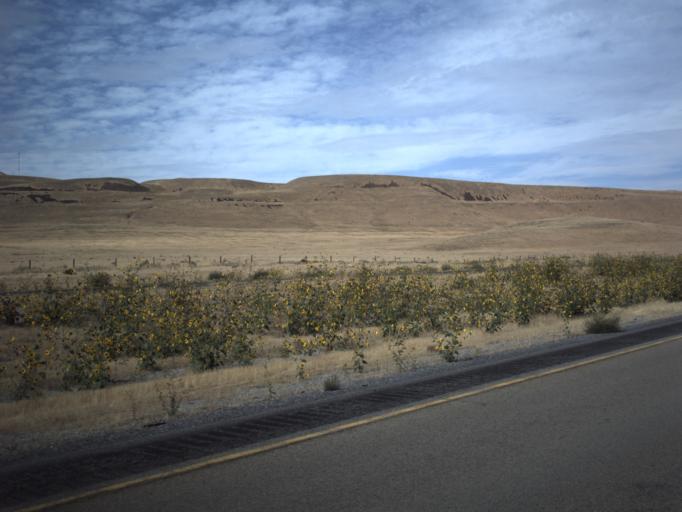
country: US
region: Utah
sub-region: Tooele County
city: Grantsville
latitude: 40.8083
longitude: -112.8642
